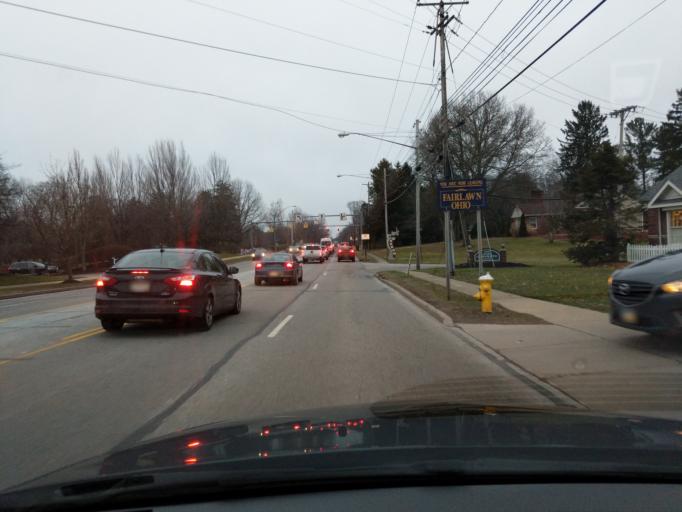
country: US
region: Ohio
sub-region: Summit County
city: Fairlawn
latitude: 41.1228
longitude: -81.5988
